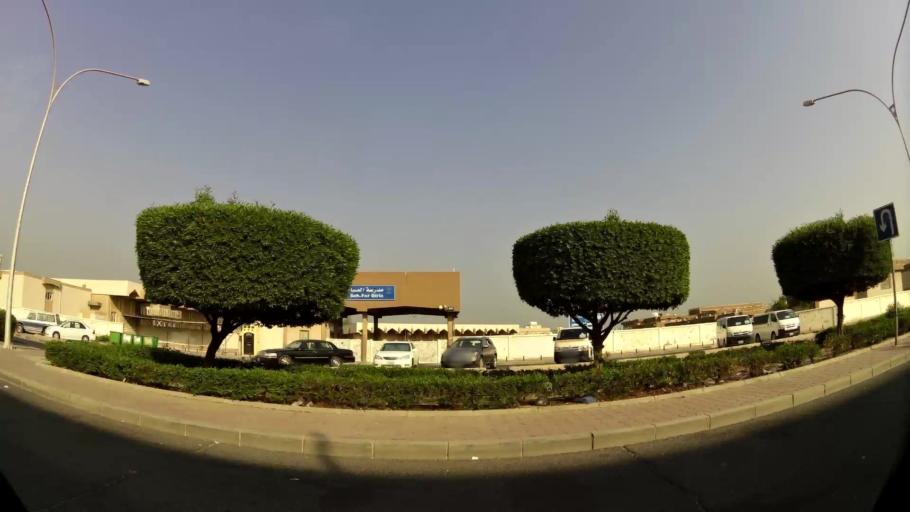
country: KW
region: Al Ahmadi
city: Al Manqaf
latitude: 29.1141
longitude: 48.1054
